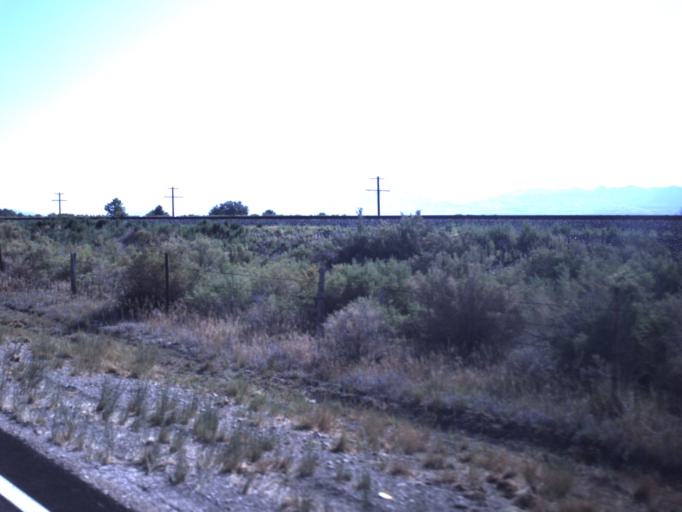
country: US
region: Utah
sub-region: Millard County
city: Delta
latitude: 39.2486
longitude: -112.6577
